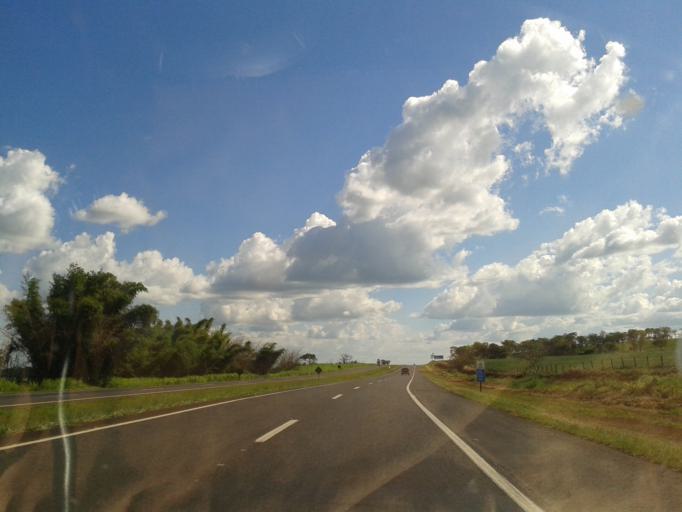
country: BR
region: Goias
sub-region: Goiatuba
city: Goiatuba
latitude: -18.0899
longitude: -49.2709
